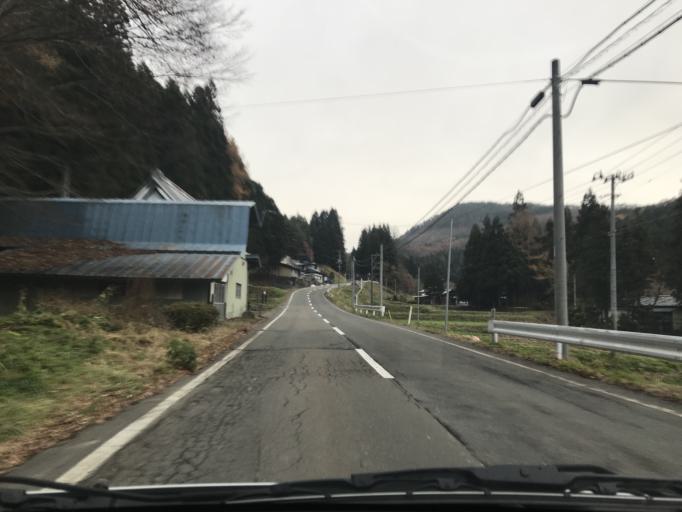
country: JP
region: Iwate
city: Tono
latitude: 39.1914
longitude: 141.3508
